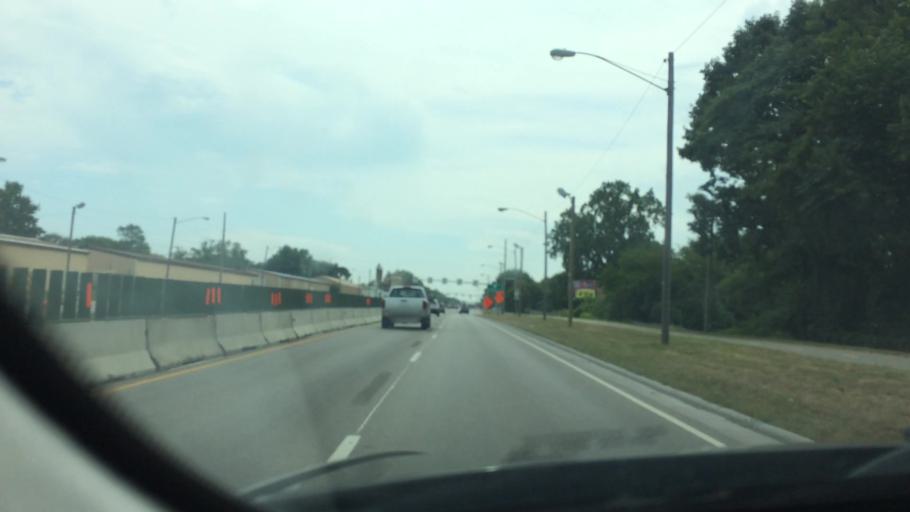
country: US
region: Ohio
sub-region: Lucas County
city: Toledo
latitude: 41.6369
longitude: -83.5584
